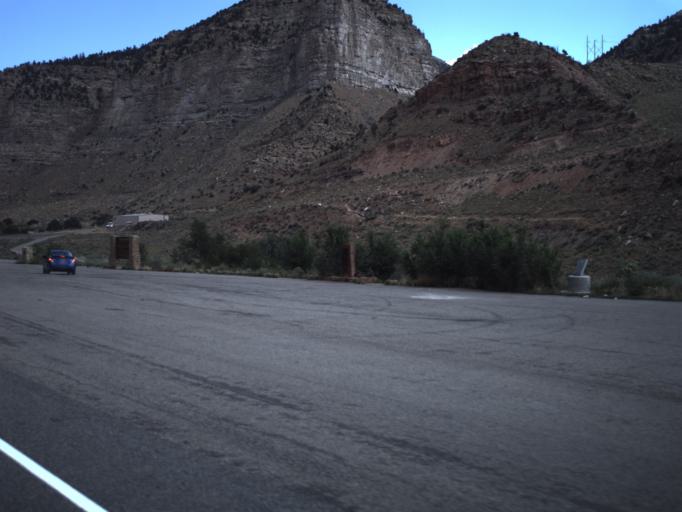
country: US
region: Utah
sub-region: Carbon County
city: Helper
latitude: 39.7315
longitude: -110.8705
